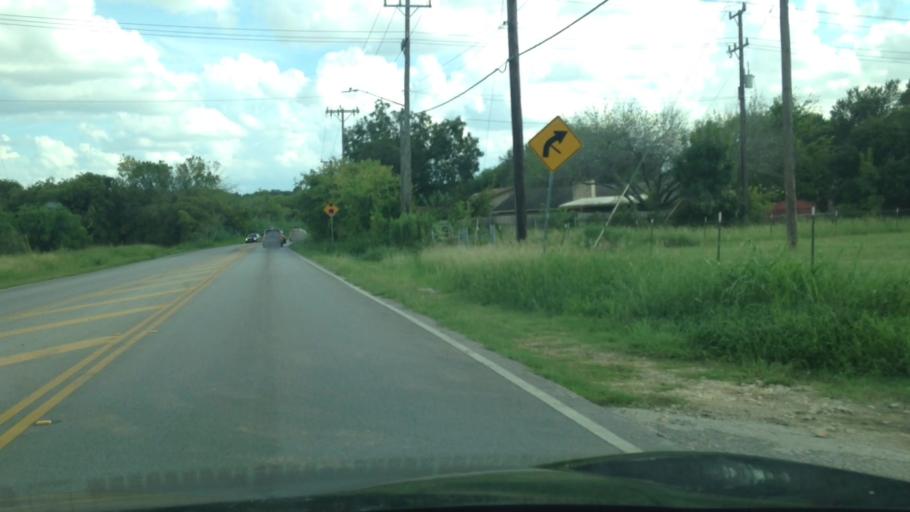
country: US
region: Texas
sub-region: Bexar County
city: Live Oak
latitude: 29.5825
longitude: -98.4038
